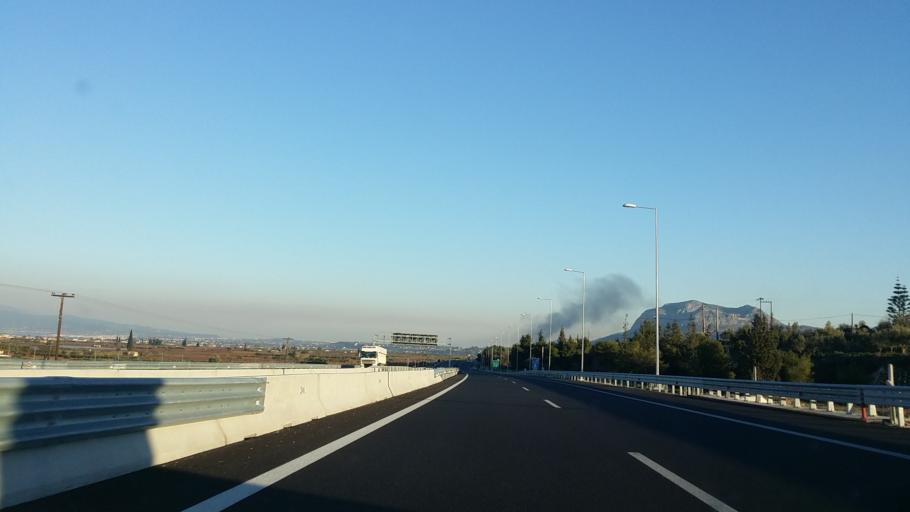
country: GR
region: Peloponnese
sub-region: Nomos Korinthias
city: Zevgolateio
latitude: 37.9229
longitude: 22.8071
